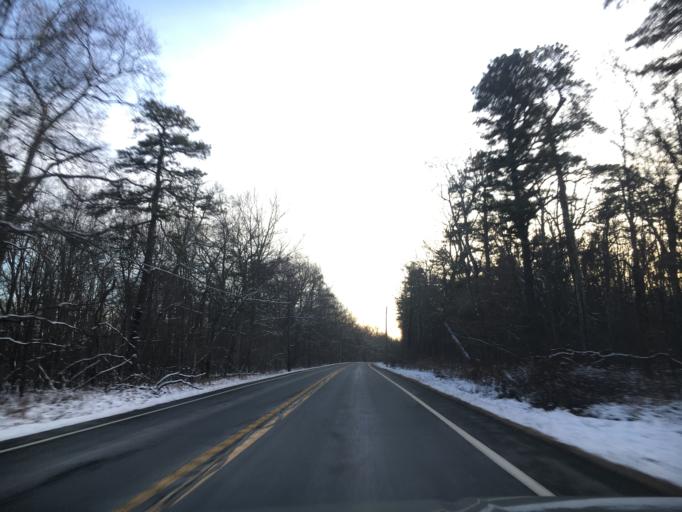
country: US
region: Pennsylvania
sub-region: Pike County
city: Hemlock Farms
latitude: 41.2311
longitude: -75.0754
